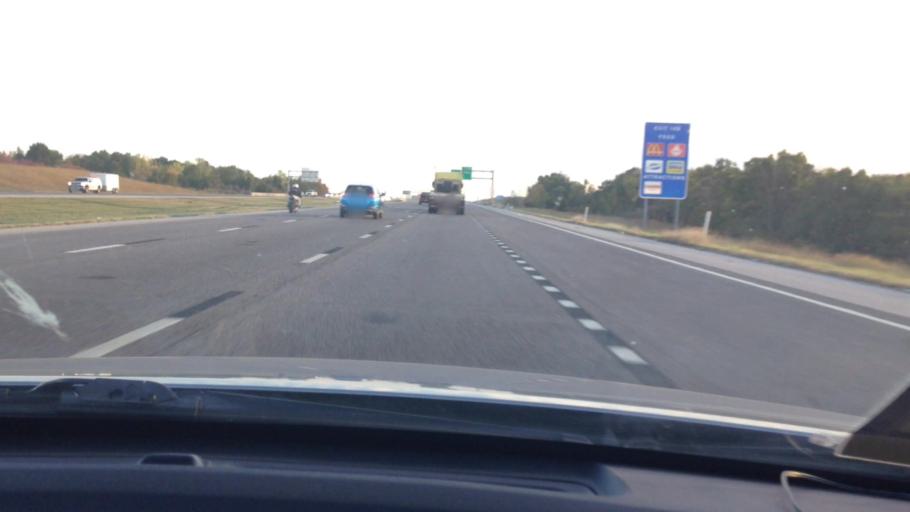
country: US
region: Kansas
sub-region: Wyandotte County
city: Edwardsville
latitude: 39.1383
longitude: -94.8196
